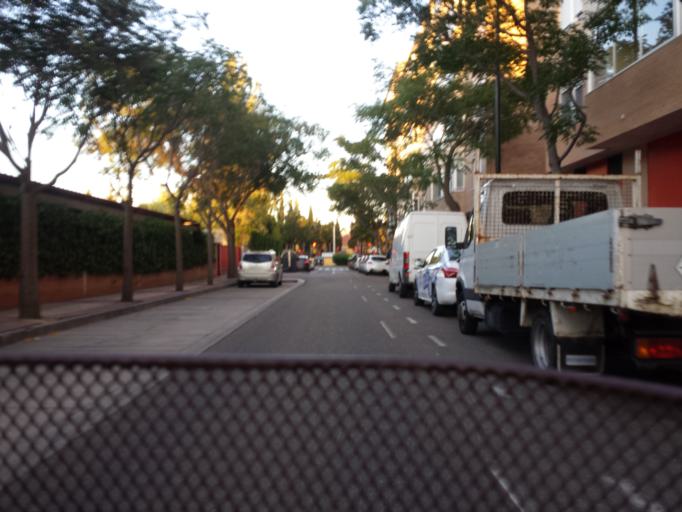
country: ES
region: Aragon
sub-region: Provincia de Zaragoza
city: Zaragoza
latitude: 41.6841
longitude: -0.8722
